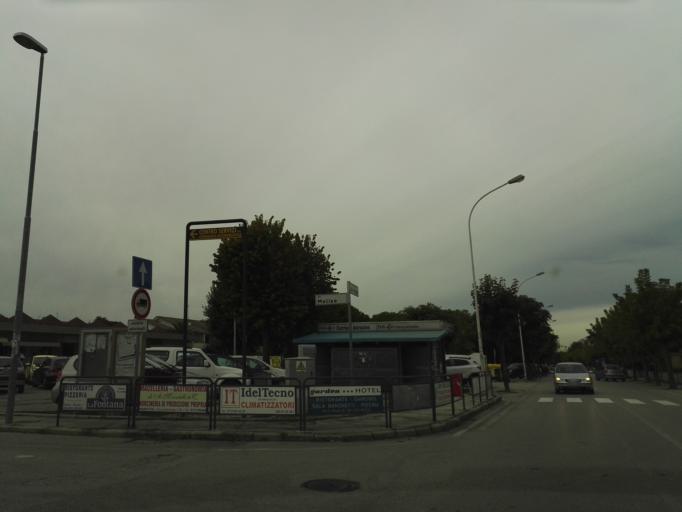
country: IT
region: The Marches
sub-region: Provincia di Pesaro e Urbino
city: Marotta
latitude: 43.7669
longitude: 13.1362
